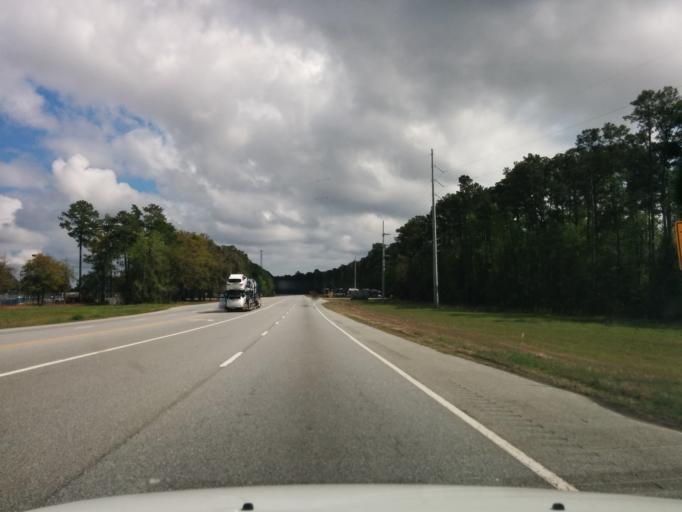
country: US
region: Georgia
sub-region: Glynn County
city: Brunswick
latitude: 31.1190
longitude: -81.5412
